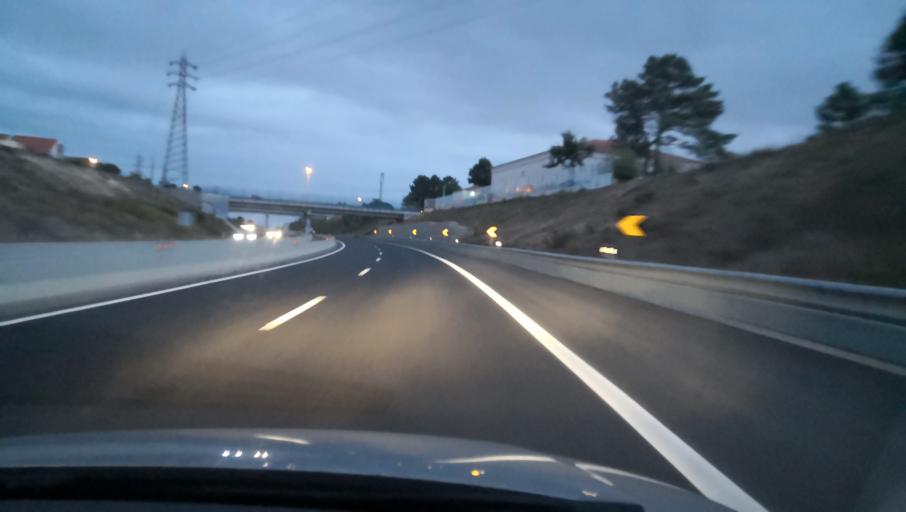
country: PT
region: Setubal
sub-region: Seixal
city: Arrentela
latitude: 38.5910
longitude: -9.0962
